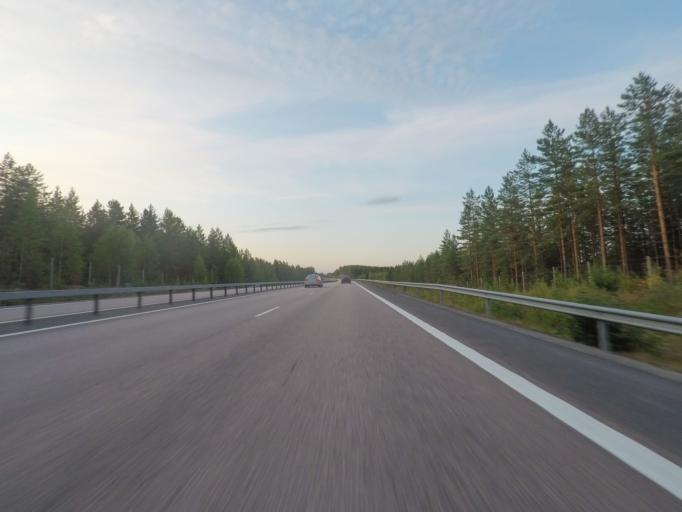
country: FI
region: Central Finland
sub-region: Jyvaeskylae
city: Saeynaetsalo
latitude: 62.1630
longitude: 25.9003
